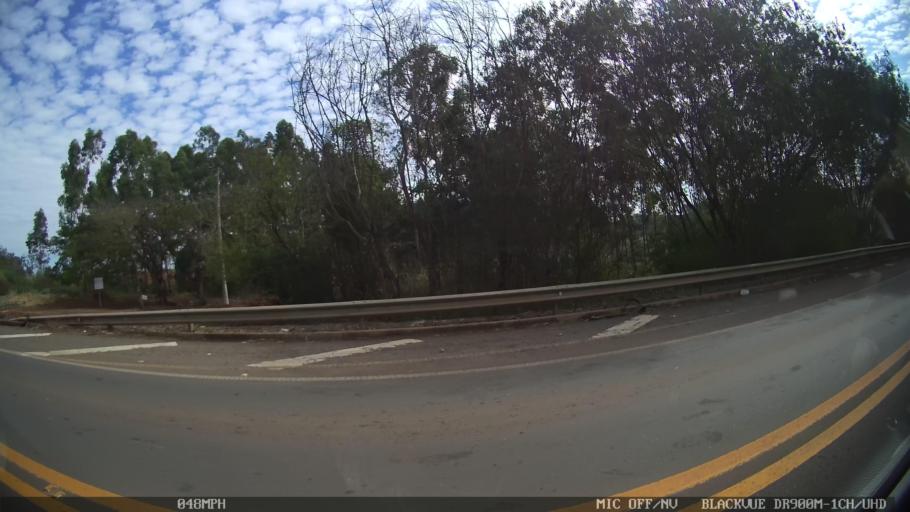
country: BR
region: Sao Paulo
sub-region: Santa Barbara D'Oeste
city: Santa Barbara d'Oeste
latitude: -22.7365
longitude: -47.4238
